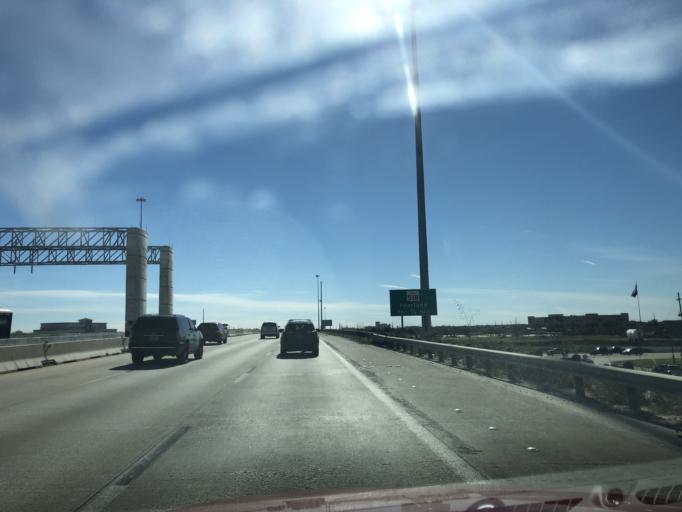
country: US
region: Texas
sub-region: Brazoria County
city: Brookside Village
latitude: 29.5816
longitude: -95.3866
